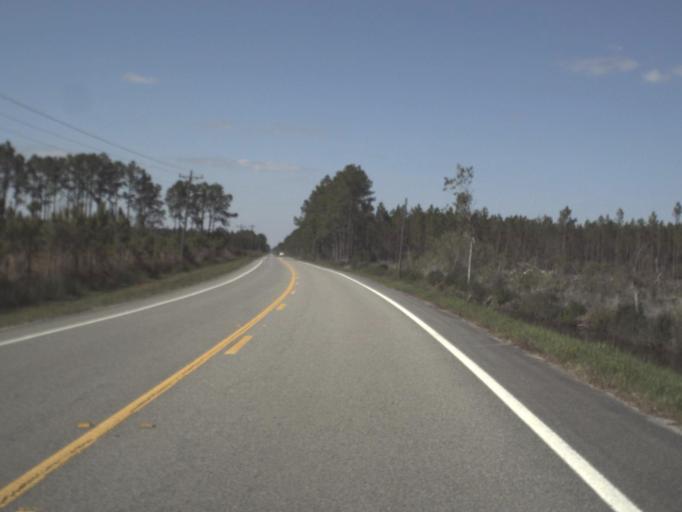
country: US
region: Florida
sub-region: Gulf County
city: Wewahitchka
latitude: 29.9796
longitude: -85.1663
